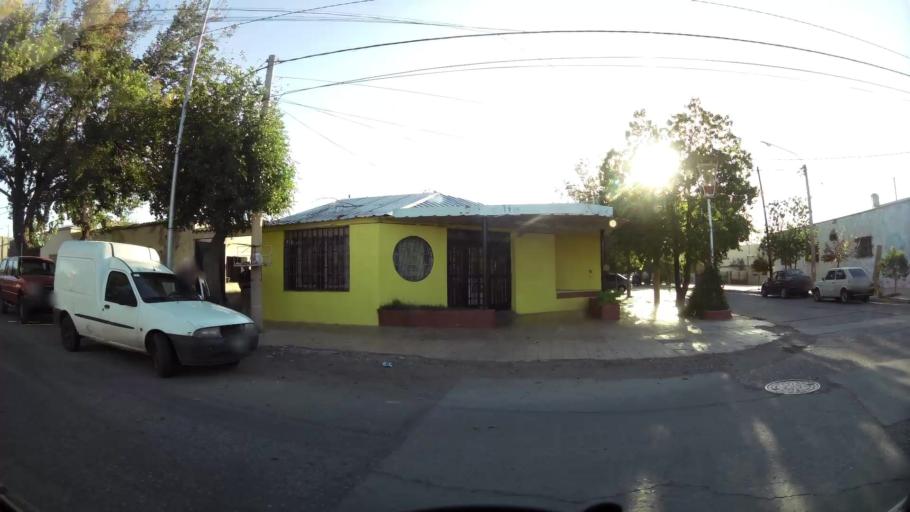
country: AR
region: San Juan
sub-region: Departamento de Santa Lucia
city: Santa Lucia
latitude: -31.5443
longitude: -68.5142
